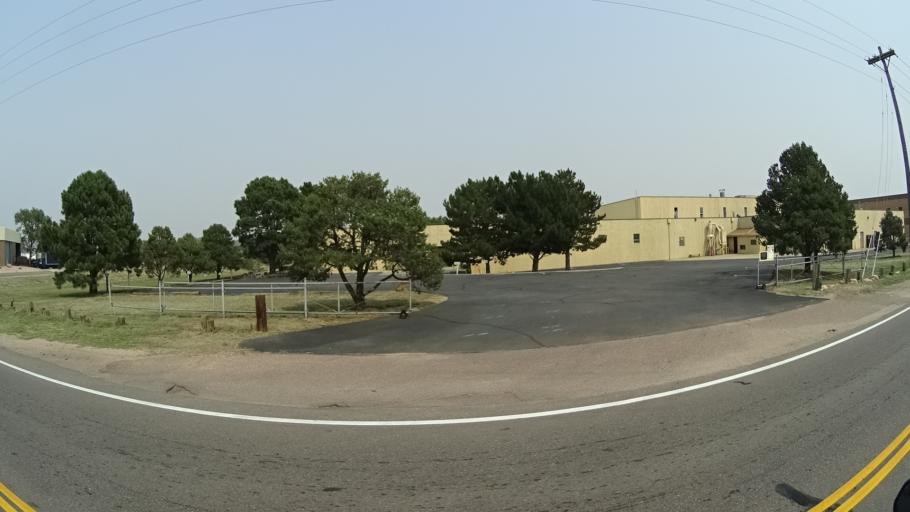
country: US
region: Colorado
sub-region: El Paso County
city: Stratmoor
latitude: 38.7882
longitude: -104.7915
